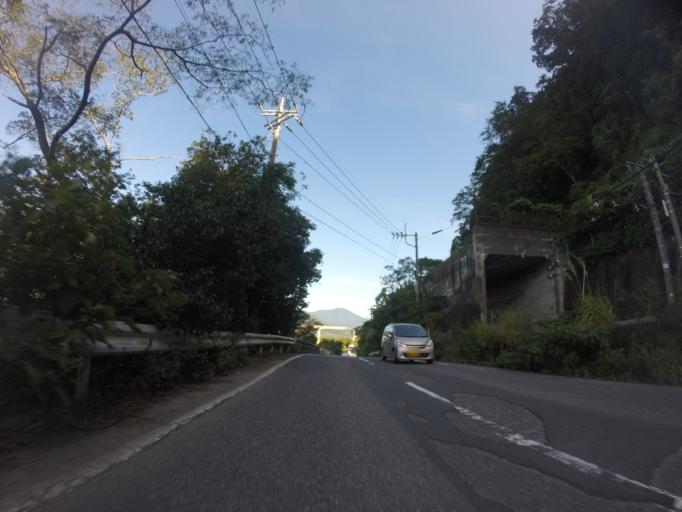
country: JP
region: Shizuoka
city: Fujinomiya
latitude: 35.3069
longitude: 138.4559
